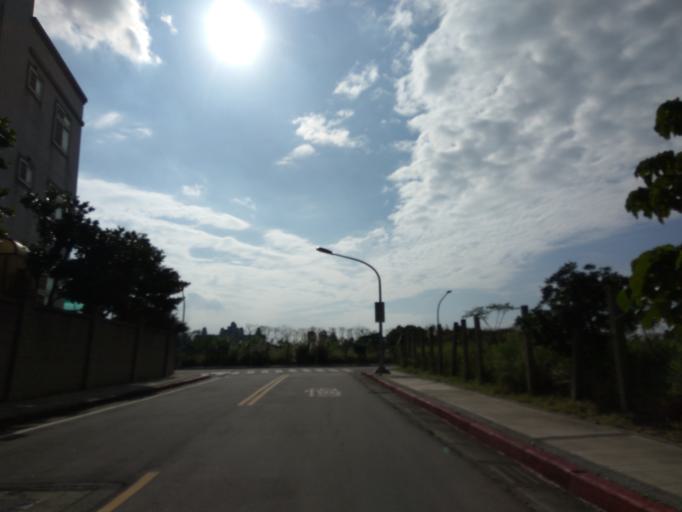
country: TW
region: Taiwan
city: Taoyuan City
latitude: 25.0506
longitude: 121.1748
